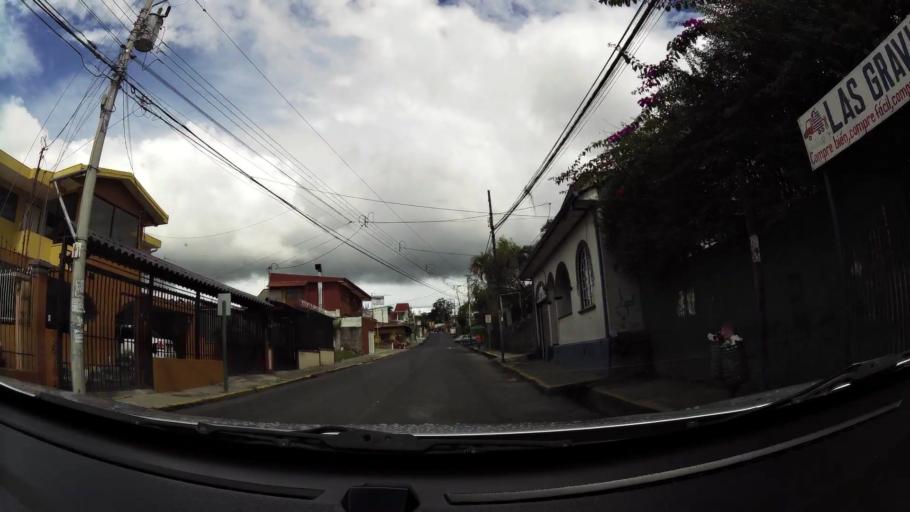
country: CR
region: Cartago
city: Tres Rios
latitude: 9.9091
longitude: -83.9848
